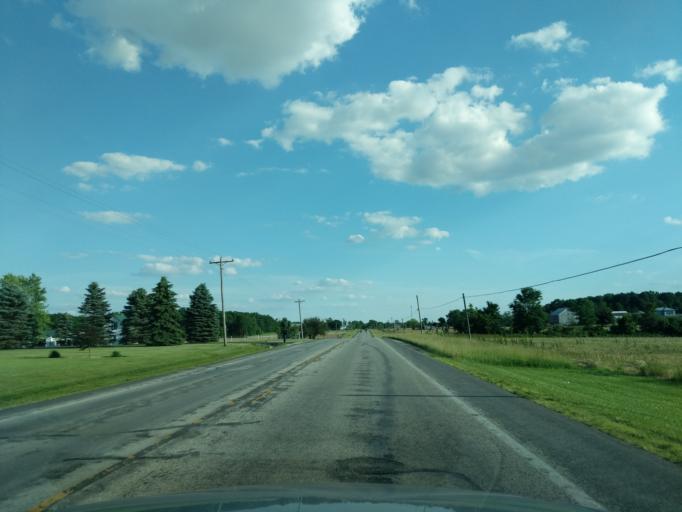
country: US
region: Indiana
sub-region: Whitley County
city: Columbia City
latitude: 41.1012
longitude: -85.4715
